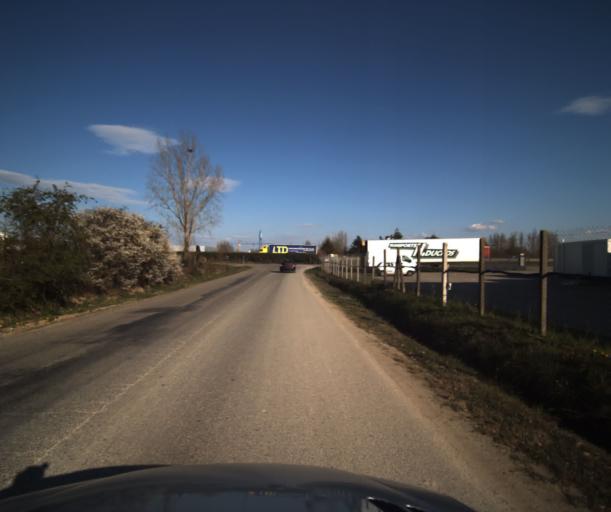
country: FR
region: Midi-Pyrenees
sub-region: Departement du Tarn-et-Garonne
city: Bressols
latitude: 43.9365
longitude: 1.3194
